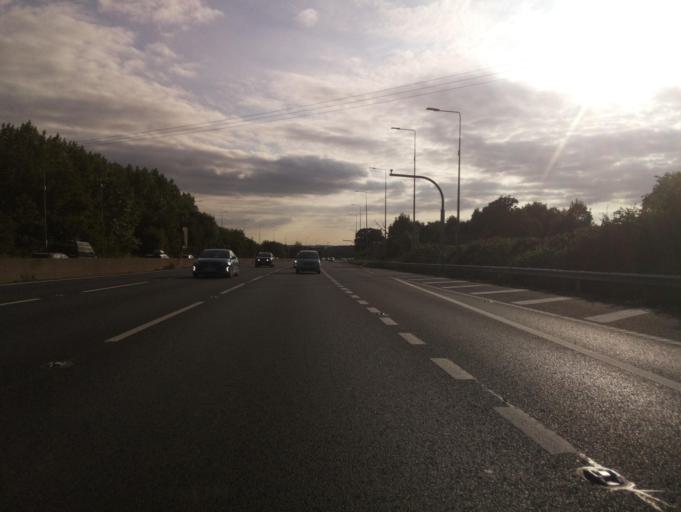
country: GB
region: England
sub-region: South Gloucestershire
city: Almondsbury
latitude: 51.5329
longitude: -2.5961
